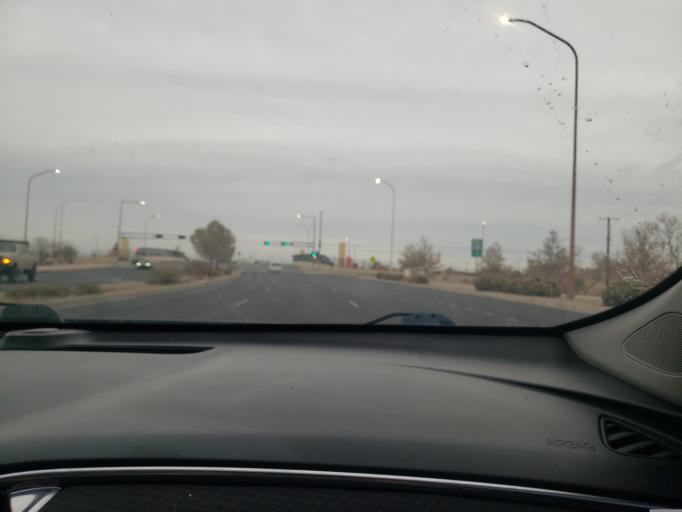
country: US
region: New Mexico
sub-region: Bernalillo County
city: Albuquerque
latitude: 35.1023
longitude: -106.5864
